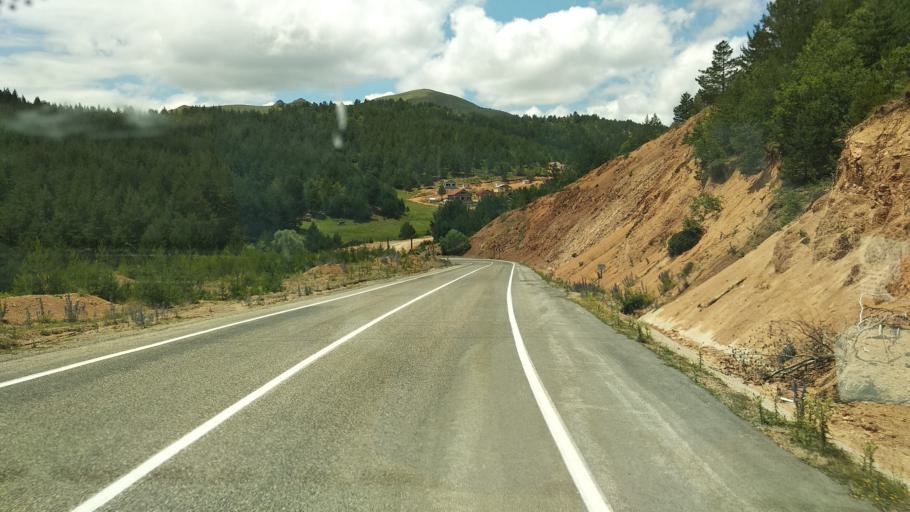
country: TR
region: Gumushane
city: Kose
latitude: 40.2950
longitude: 39.5711
